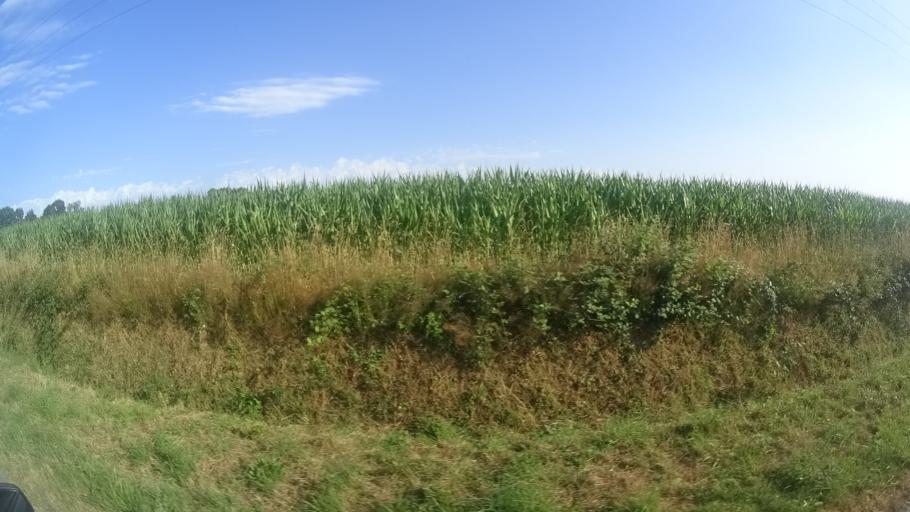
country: FR
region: Brittany
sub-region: Departement du Morbihan
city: Beganne
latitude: 47.6098
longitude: -2.2127
